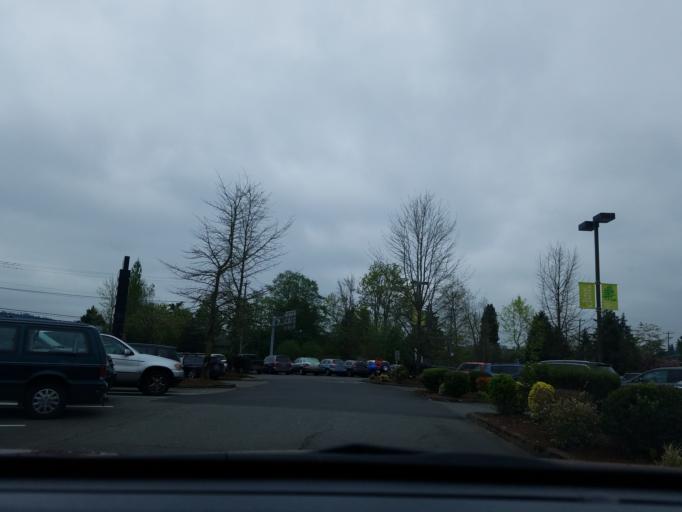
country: US
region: Washington
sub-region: King County
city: Lake Forest Park
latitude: 47.7532
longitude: -122.2792
